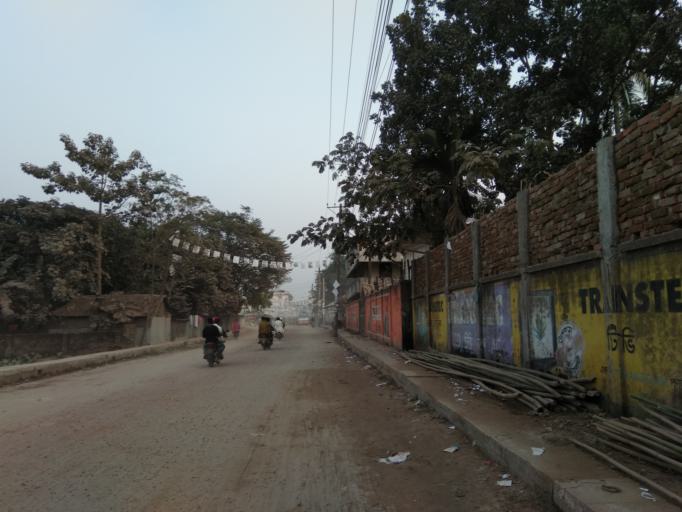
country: BD
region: Rangpur Division
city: Rangpur
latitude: 25.7323
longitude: 89.2630
